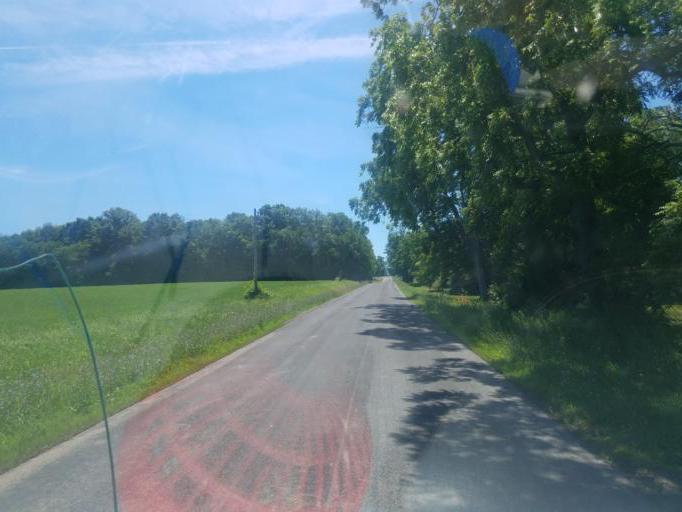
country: US
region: New York
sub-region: Yates County
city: Penn Yan
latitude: 42.6371
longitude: -77.0160
